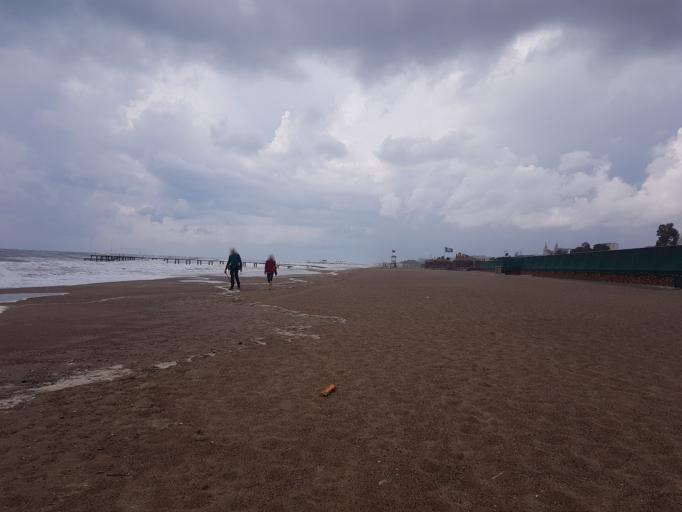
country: TR
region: Antalya
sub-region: Serik
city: Kumkoey
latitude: 36.8537
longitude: 30.9035
